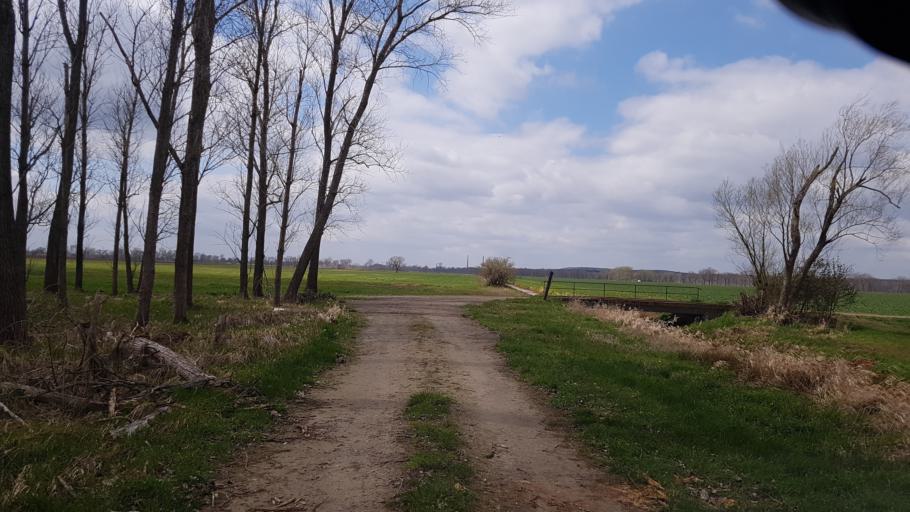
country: DE
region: Brandenburg
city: Schraden
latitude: 51.4667
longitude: 13.6814
